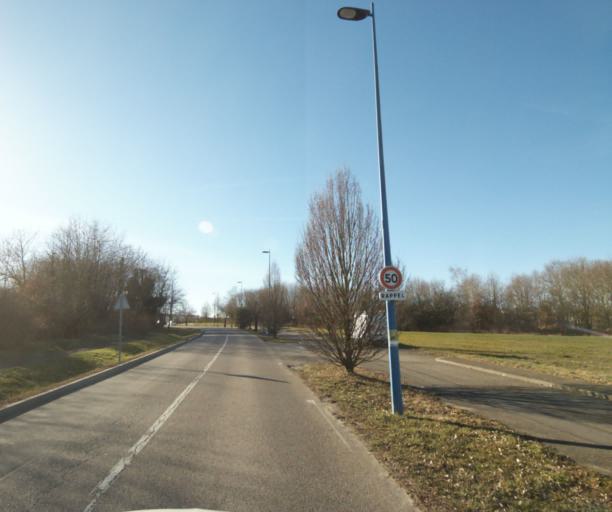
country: FR
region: Lorraine
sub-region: Departement de Meurthe-et-Moselle
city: Heillecourt
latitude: 48.6584
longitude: 6.2139
